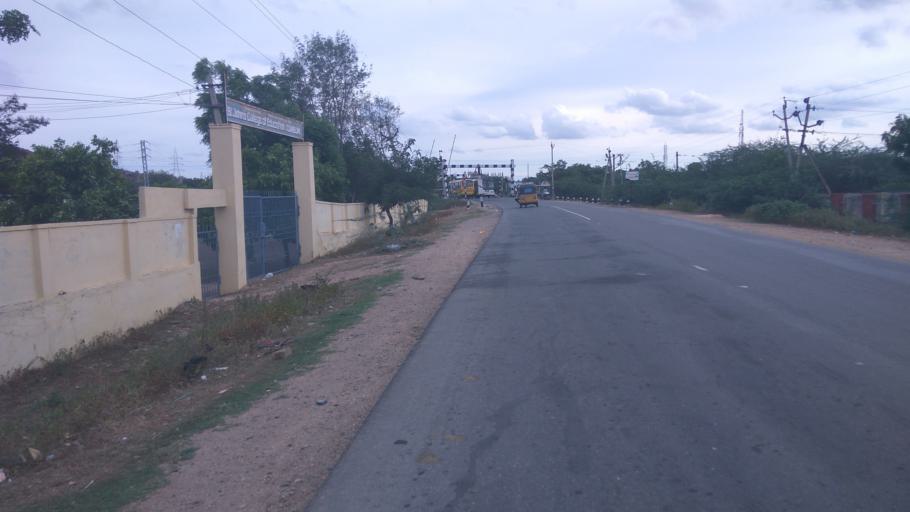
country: IN
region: Andhra Pradesh
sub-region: Prakasam
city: Cumbum
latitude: 15.5944
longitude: 79.1165
